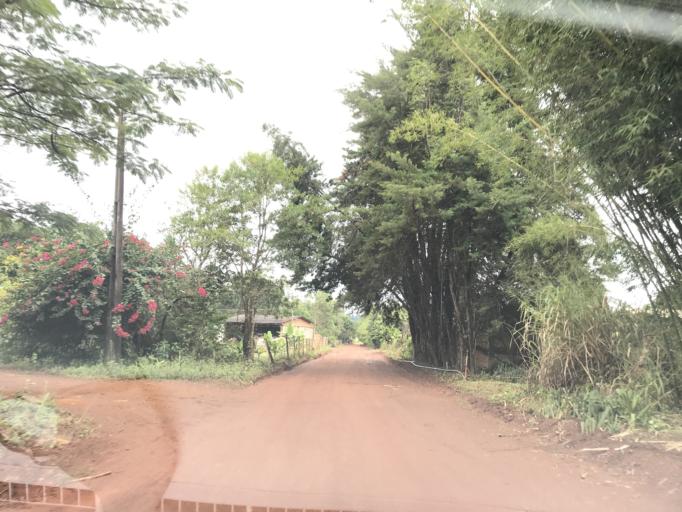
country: BR
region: Federal District
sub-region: Brasilia
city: Brasilia
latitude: -15.9185
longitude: -47.9292
